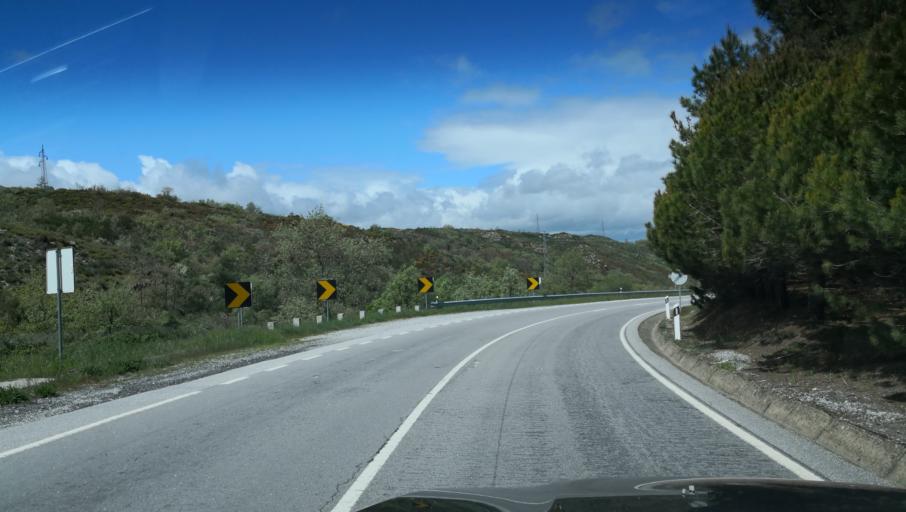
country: PT
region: Vila Real
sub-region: Vila Real
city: Vila Real
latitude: 41.3983
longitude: -7.7012
